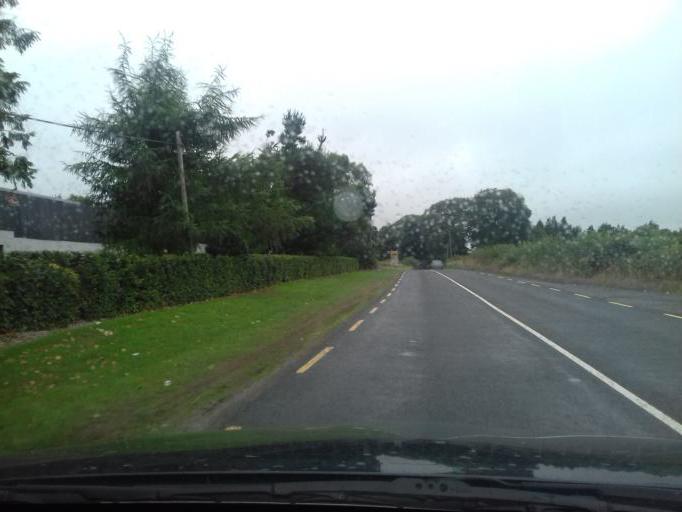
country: IE
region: Leinster
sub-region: Kilkenny
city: Graiguenamanagh
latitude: 52.6169
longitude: -6.9373
